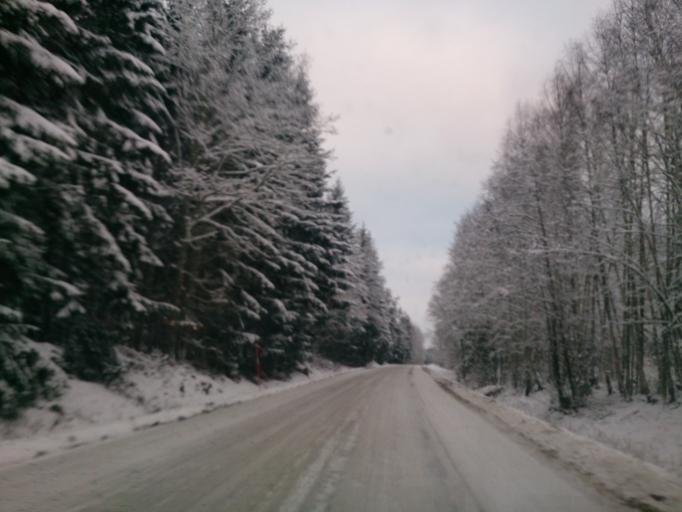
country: SE
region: OEstergoetland
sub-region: Atvidabergs Kommun
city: Atvidaberg
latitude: 58.2966
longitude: 16.0071
